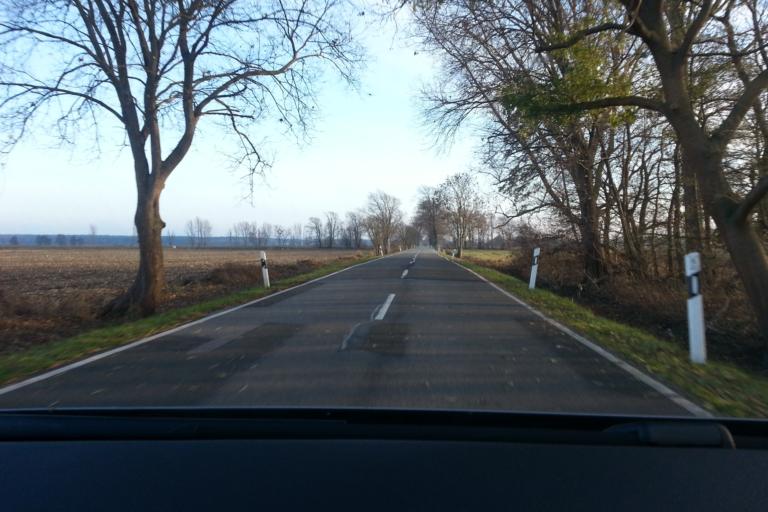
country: DE
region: Mecklenburg-Vorpommern
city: Strasburg
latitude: 53.6295
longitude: 13.7590
